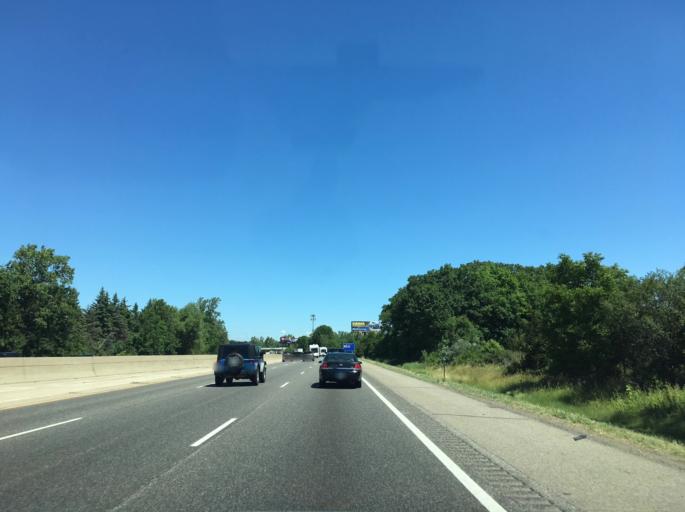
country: US
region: Michigan
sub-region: Genesee County
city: Flint
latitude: 43.0417
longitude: -83.7535
